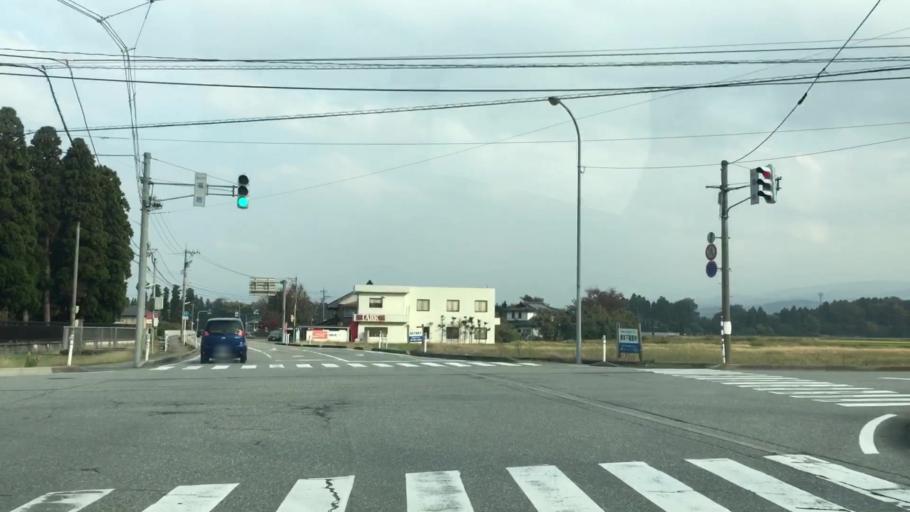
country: JP
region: Toyama
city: Yatsuomachi-higashikumisaka
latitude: 36.6128
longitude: 137.1917
